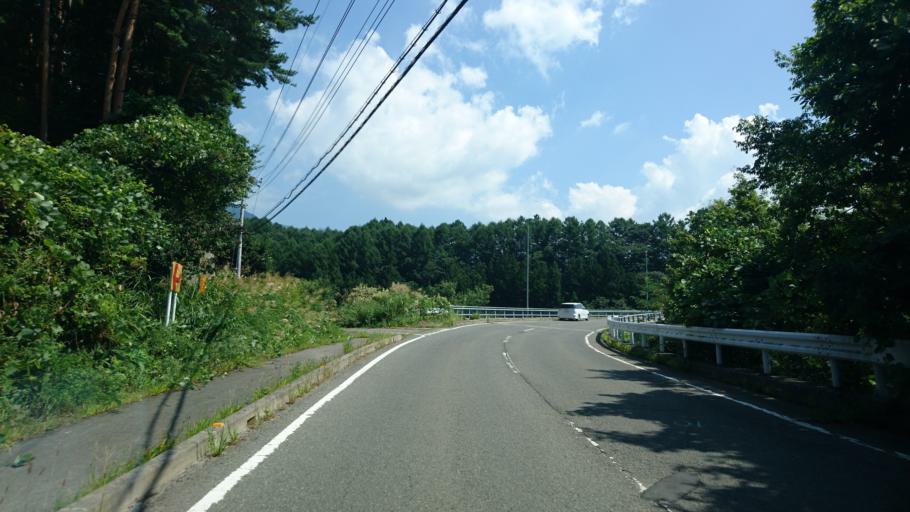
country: JP
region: Gunma
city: Numata
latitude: 36.7611
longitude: 139.2380
